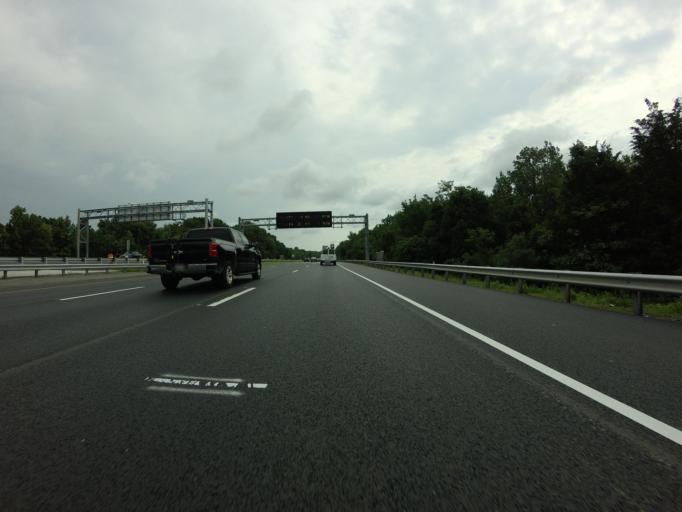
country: US
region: Maryland
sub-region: Harford County
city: Aberdeen
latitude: 39.5468
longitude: -76.1663
